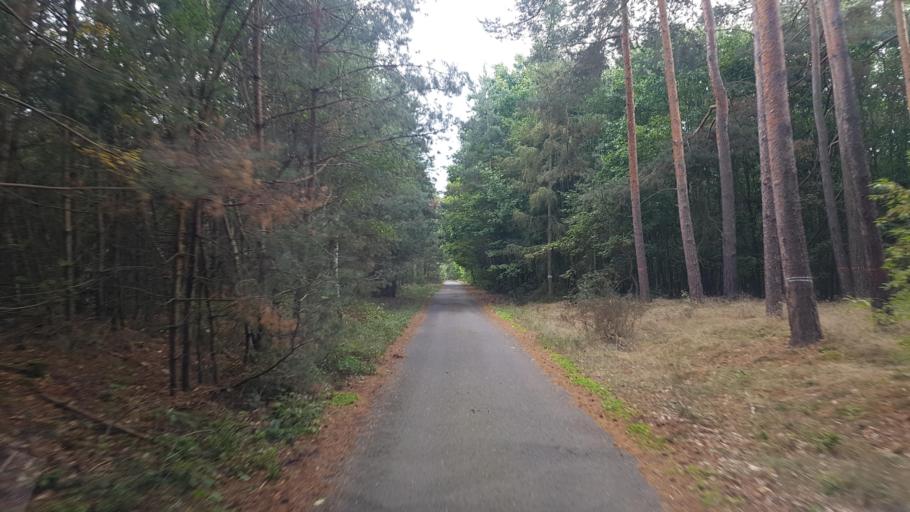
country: DE
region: Brandenburg
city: Ihlow
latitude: 51.8630
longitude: 13.2580
